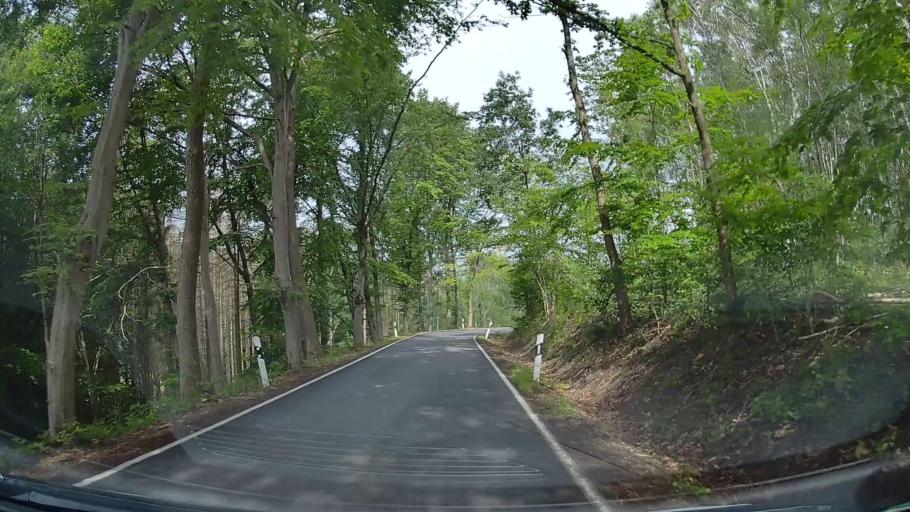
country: DE
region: North Rhine-Westphalia
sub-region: Regierungsbezirk Detmold
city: Barntrup
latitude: 52.0915
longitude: 9.1305
